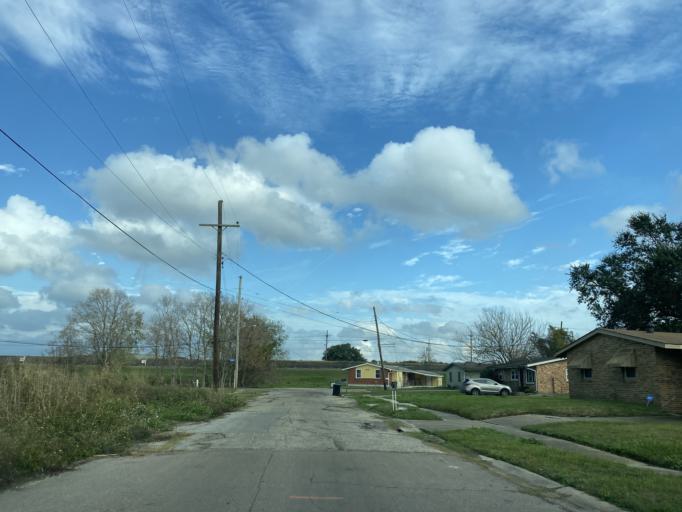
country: US
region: Louisiana
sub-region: Saint Bernard Parish
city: Arabi
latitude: 30.0242
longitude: -90.0369
